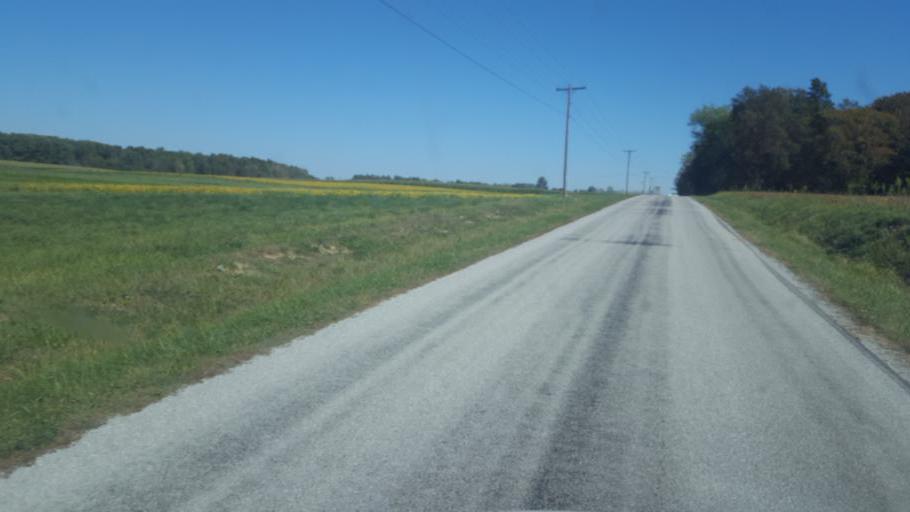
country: US
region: Ohio
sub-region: Huron County
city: Greenwich
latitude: 40.9929
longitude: -82.4536
